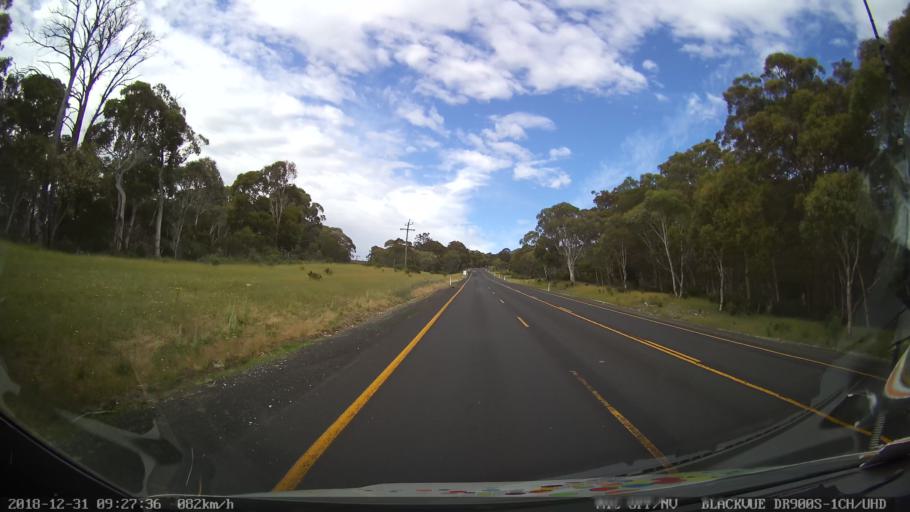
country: AU
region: New South Wales
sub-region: Snowy River
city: Jindabyne
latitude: -36.4573
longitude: 148.4826
